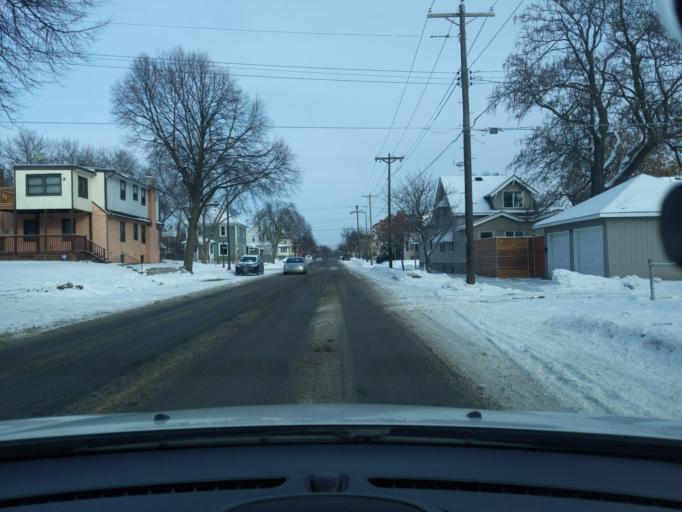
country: US
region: Minnesota
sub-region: Ramsey County
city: Saint Paul
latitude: 44.9533
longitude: -93.1364
